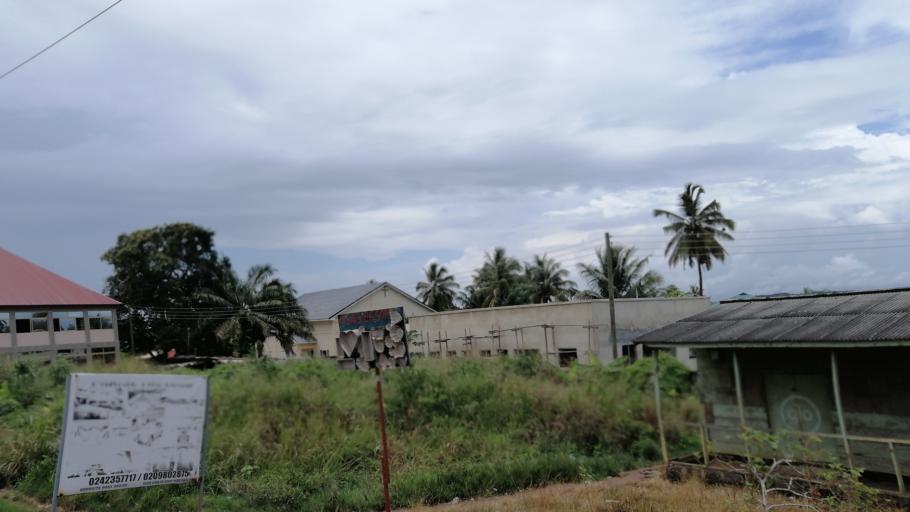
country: GH
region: Central
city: Elmina
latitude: 5.0932
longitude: -1.3454
